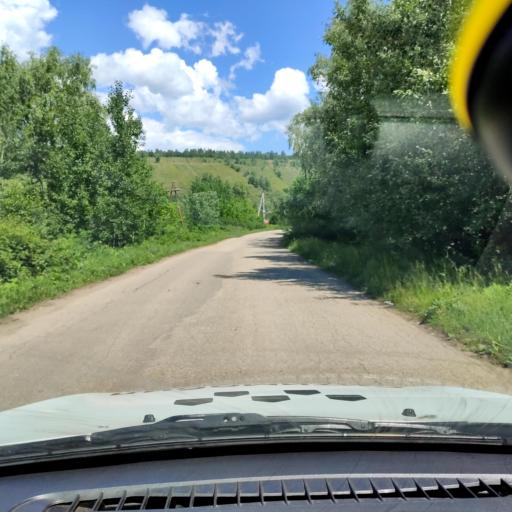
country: RU
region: Samara
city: Povolzhskiy
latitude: 53.4671
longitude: 49.6688
